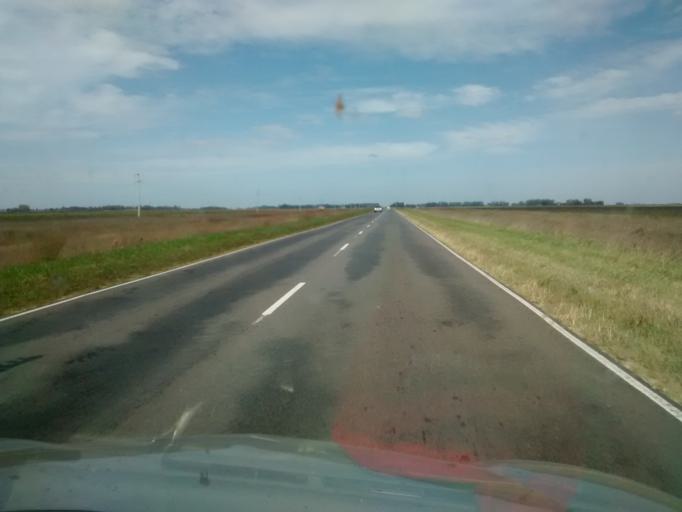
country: AR
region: Buenos Aires
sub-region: Partido de Ayacucho
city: Ayacucho
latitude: -37.0930
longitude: -58.5471
